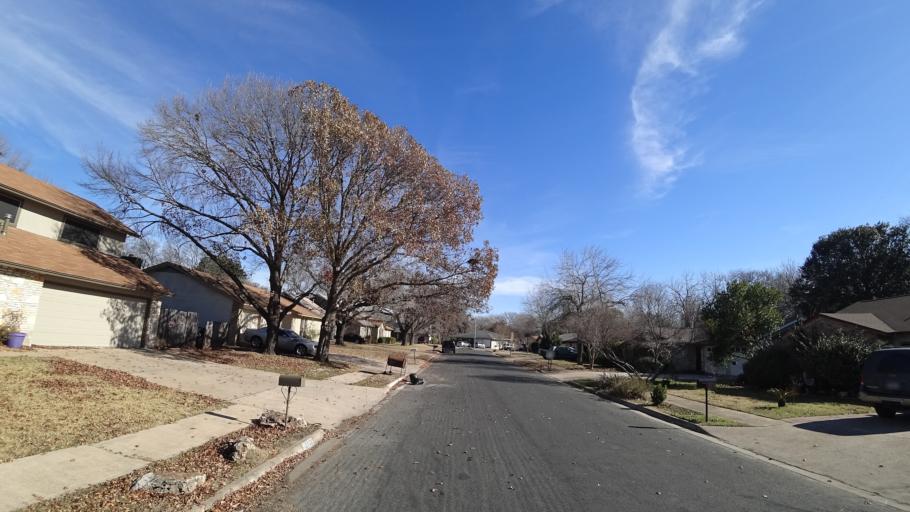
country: US
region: Texas
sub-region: Travis County
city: Wells Branch
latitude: 30.3822
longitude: -97.7013
